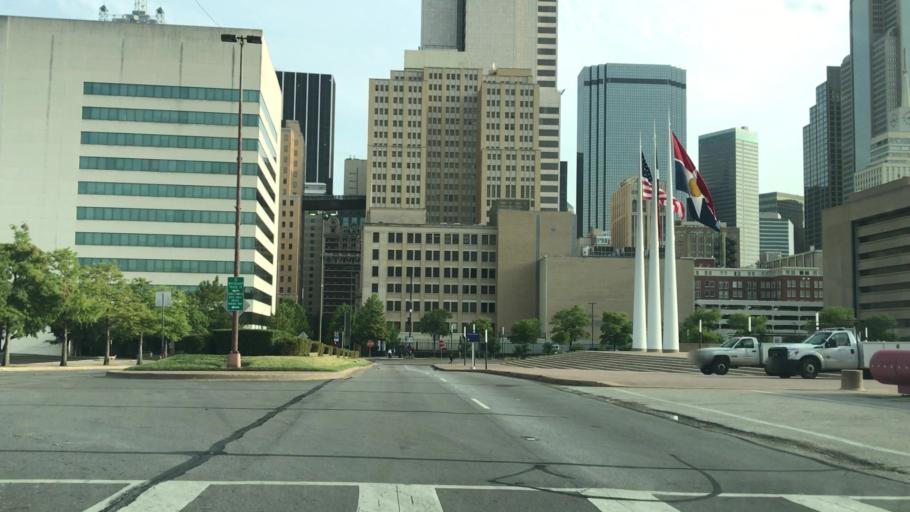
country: US
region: Texas
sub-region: Dallas County
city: Dallas
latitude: 32.7762
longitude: -96.7982
